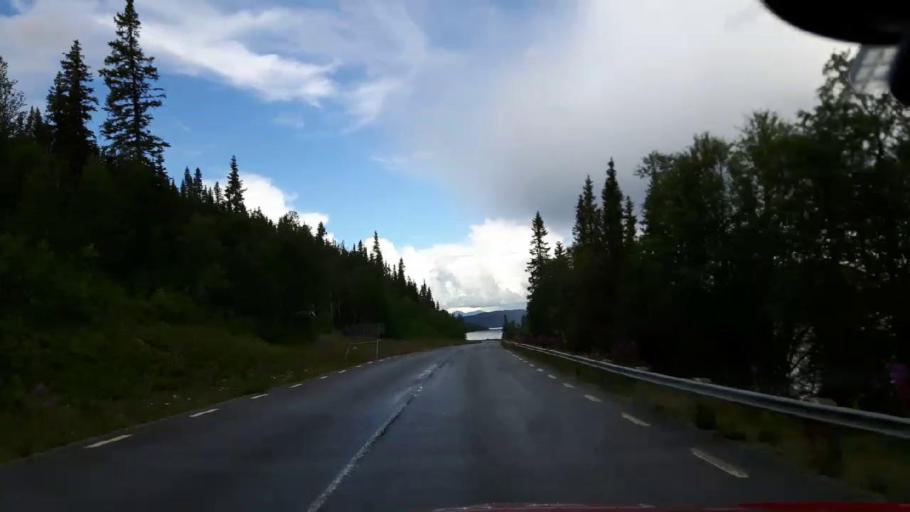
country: SE
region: Vaesterbotten
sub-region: Vilhelmina Kommun
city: Sjoberg
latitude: 64.9766
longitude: 15.3204
